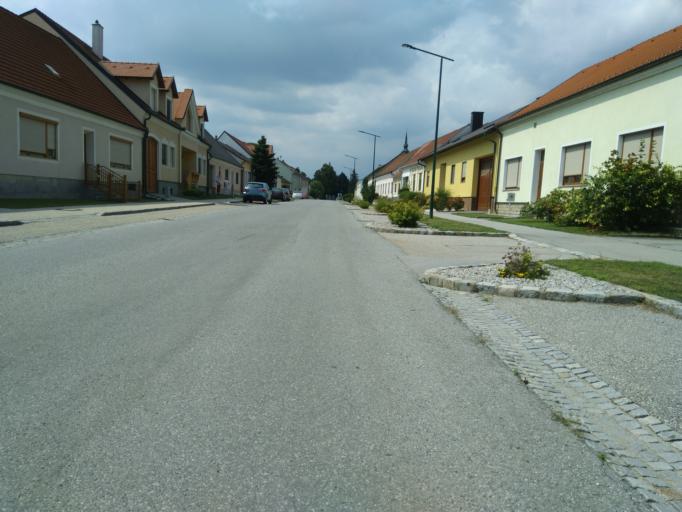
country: AT
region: Lower Austria
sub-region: Politischer Bezirk Ganserndorf
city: Ganserndorf
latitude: 48.3646
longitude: 16.7014
